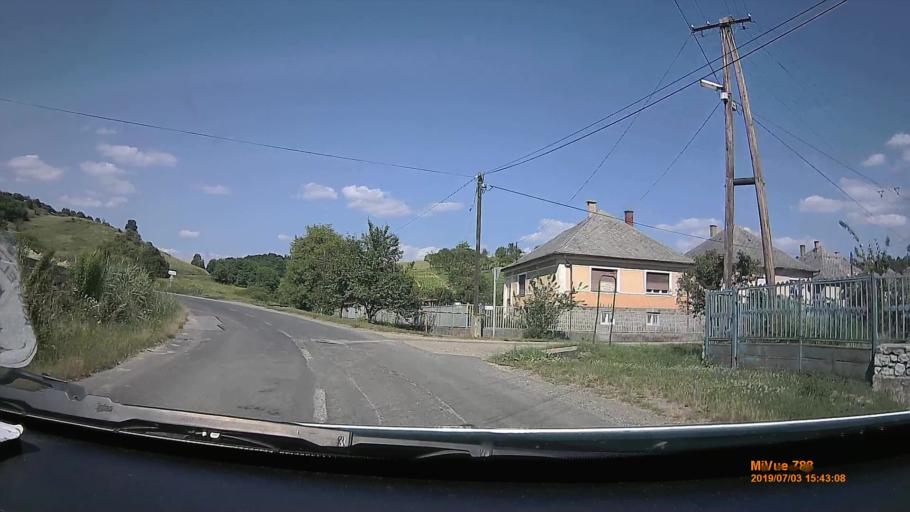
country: HU
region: Heves
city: Szilvasvarad
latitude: 48.1688
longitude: 20.4380
